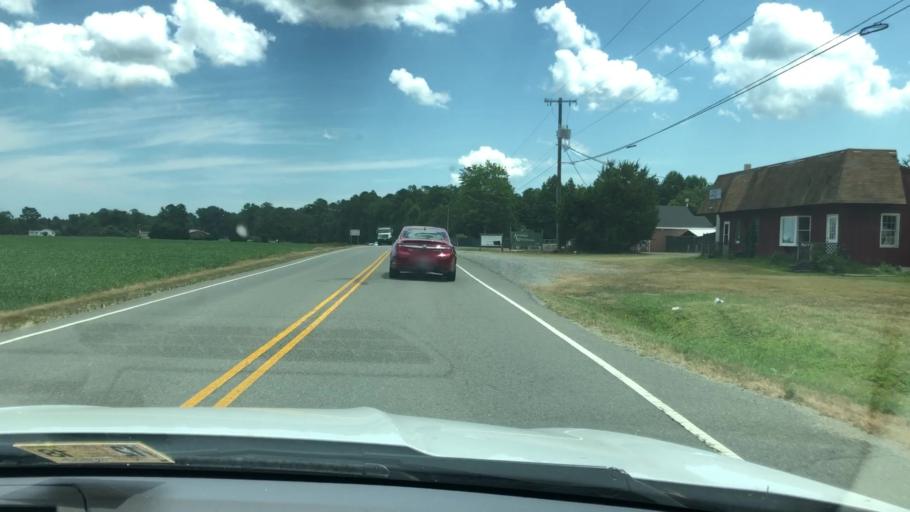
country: US
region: Virginia
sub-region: Lancaster County
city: Lancaster
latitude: 37.7701
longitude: -76.5068
